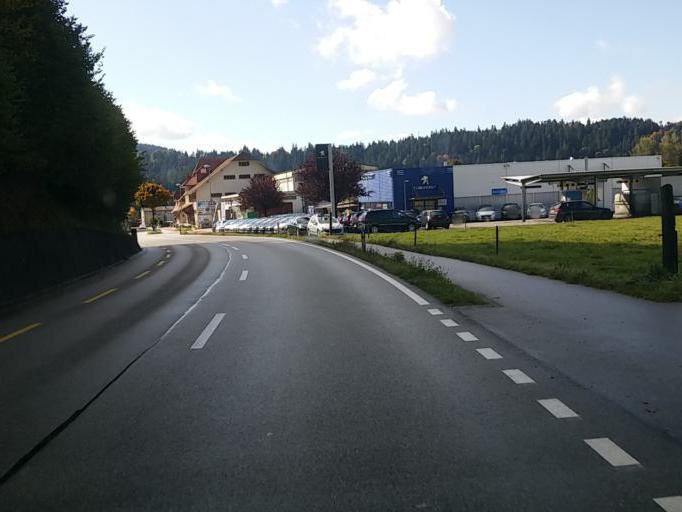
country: CH
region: Bern
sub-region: Emmental District
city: Ruderswil
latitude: 47.0016
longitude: 7.7119
